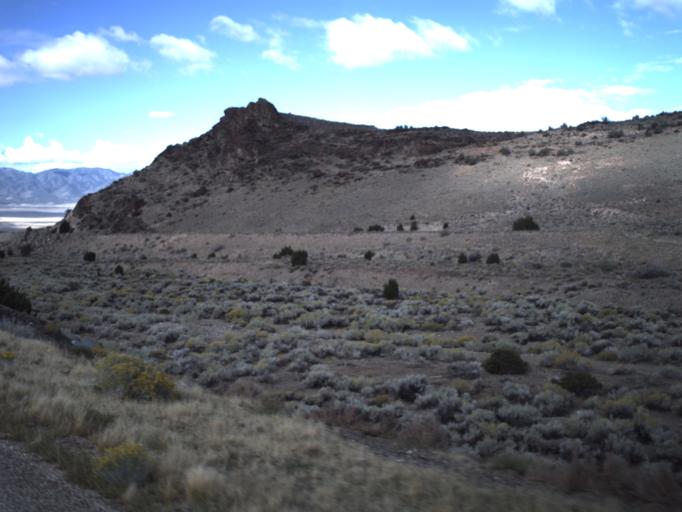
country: US
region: Utah
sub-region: Beaver County
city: Milford
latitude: 38.4361
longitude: -113.2754
